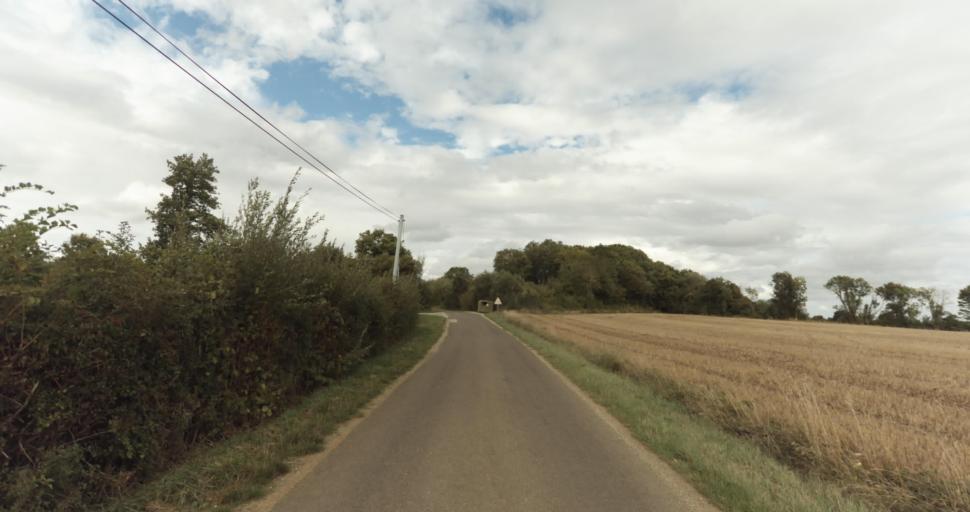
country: FR
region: Lower Normandy
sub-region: Departement de l'Orne
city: Sainte-Gauburge-Sainte-Colombe
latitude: 48.7477
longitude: 0.3778
